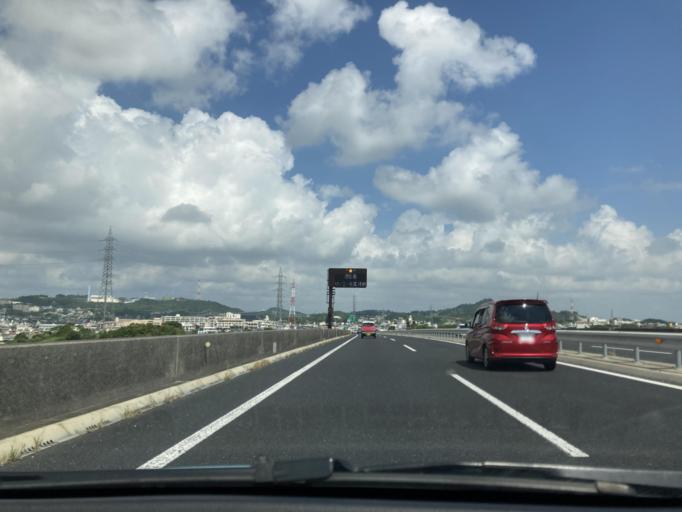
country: JP
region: Okinawa
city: Tomigusuku
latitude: 26.1911
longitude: 127.7388
